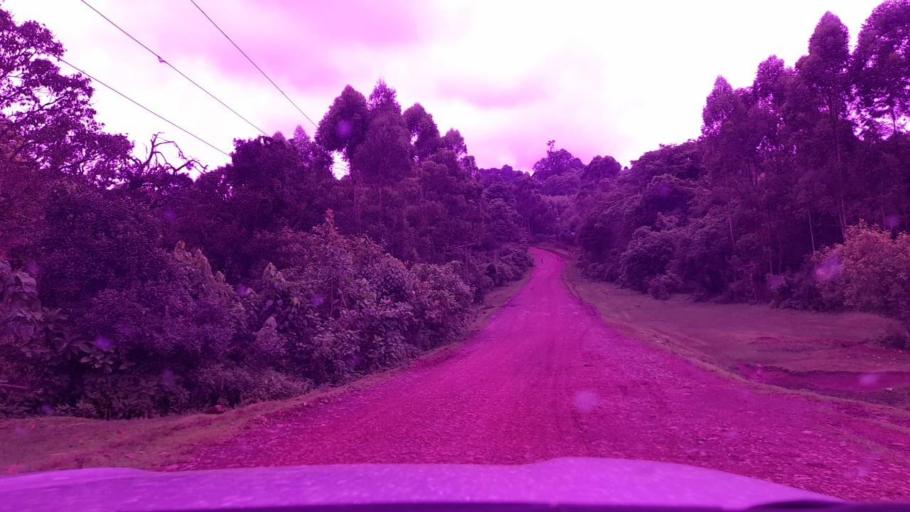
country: ET
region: Southern Nations, Nationalities, and People's Region
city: Tippi
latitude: 7.5764
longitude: 35.7795
